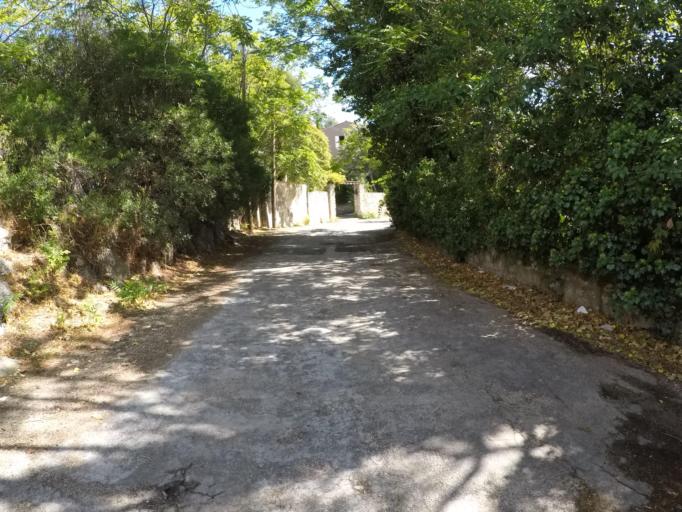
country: FR
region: Provence-Alpes-Cote d'Azur
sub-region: Departement des Bouches-du-Rhone
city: Marseille 09
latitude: 43.2491
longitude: 5.4376
